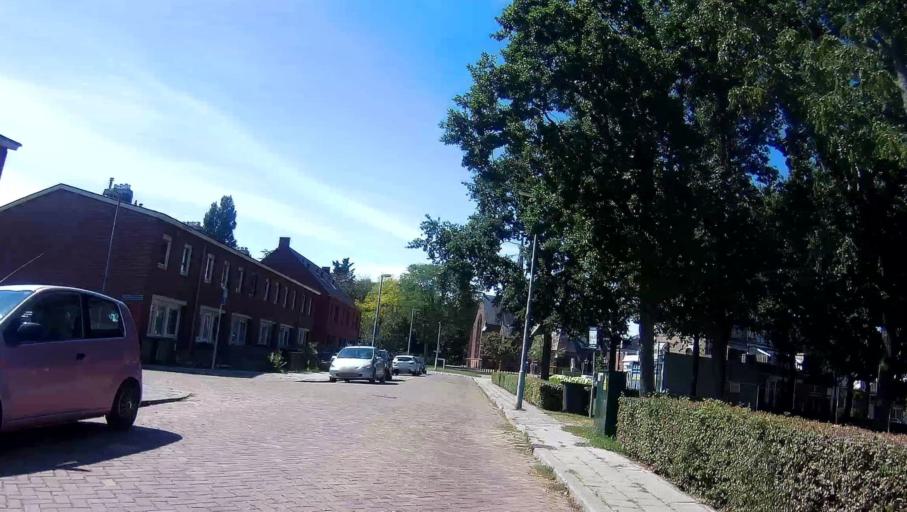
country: NL
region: South Holland
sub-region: Gemeente Capelle aan den IJssel
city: Capelle-West
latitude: 51.9003
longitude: 4.5507
